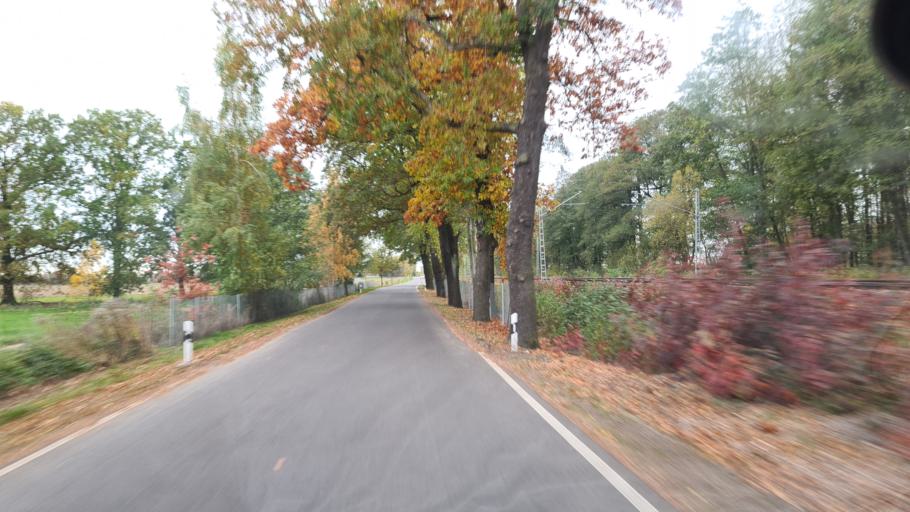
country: DE
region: Brandenburg
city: Finsterwalde
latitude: 51.6510
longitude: 13.7468
